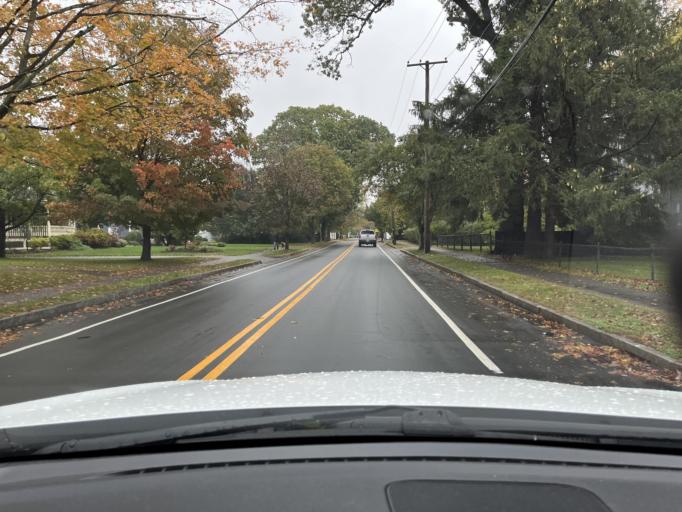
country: US
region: Massachusetts
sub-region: Norfolk County
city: Needham
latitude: 42.2802
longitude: -71.2327
